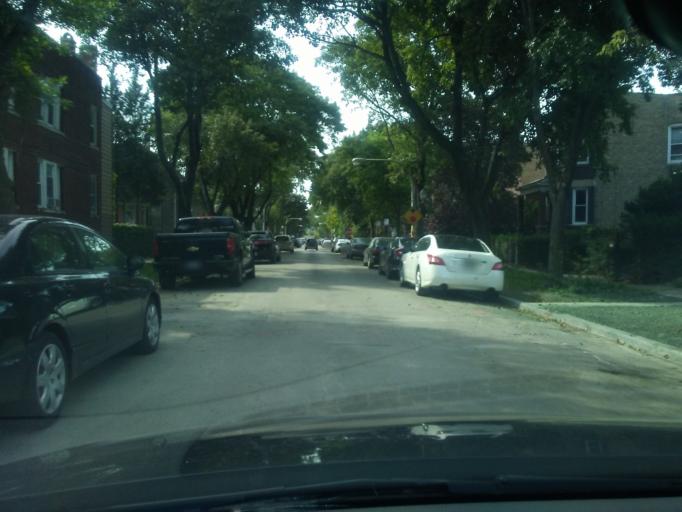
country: US
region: Illinois
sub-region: Cook County
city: Lincolnwood
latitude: 41.9385
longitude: -87.7004
